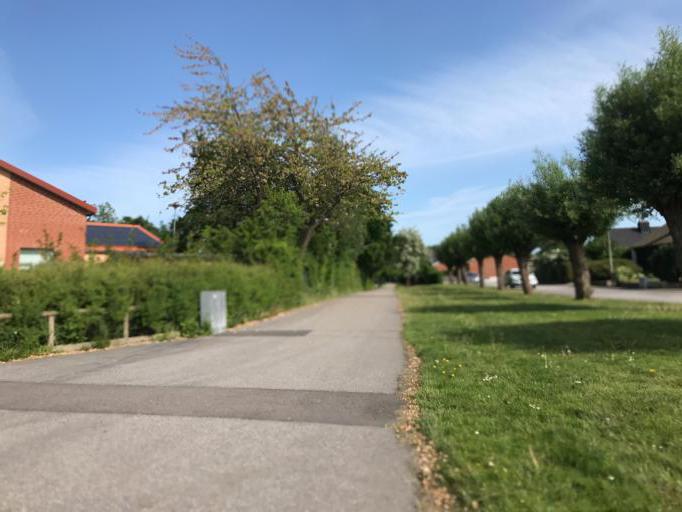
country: SE
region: Skane
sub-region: Malmo
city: Oxie
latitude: 55.5500
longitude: 13.1011
